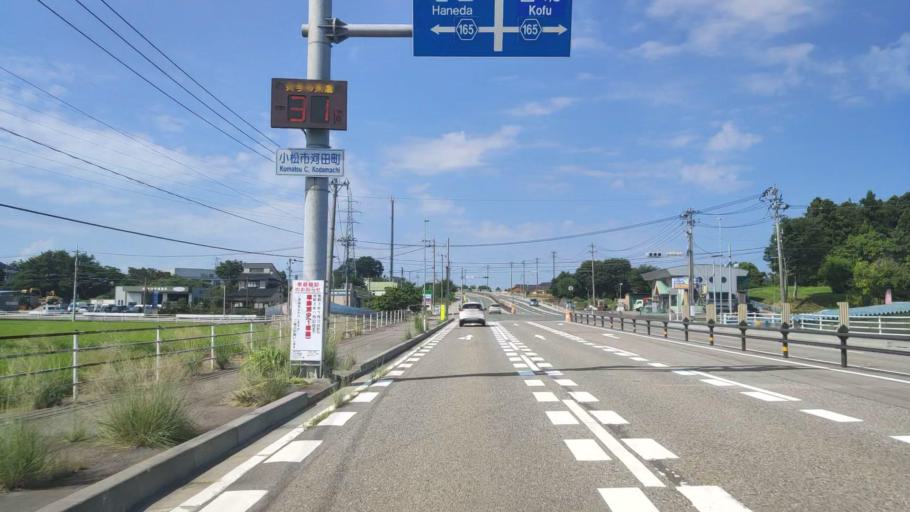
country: JP
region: Ishikawa
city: Komatsu
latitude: 36.4135
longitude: 136.5113
